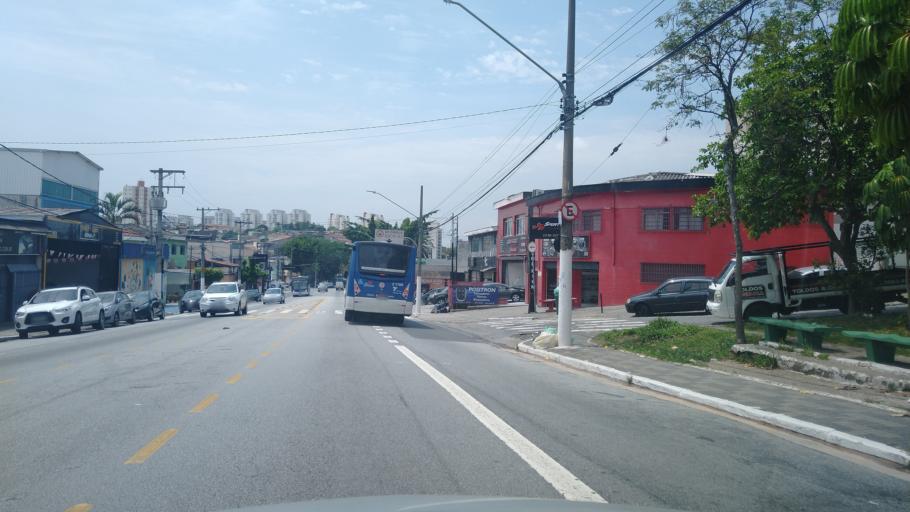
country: BR
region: Sao Paulo
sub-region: Sao Paulo
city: Sao Paulo
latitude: -23.4801
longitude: -46.6602
